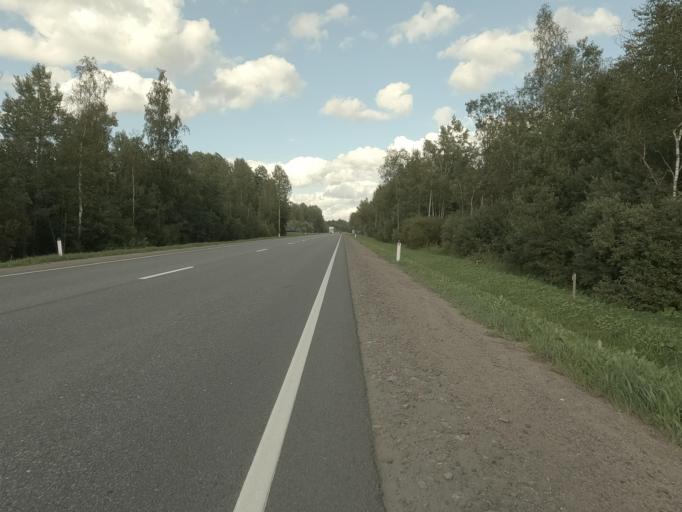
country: RU
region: Leningrad
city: Nikol'skoye
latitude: 59.6609
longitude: 30.8726
